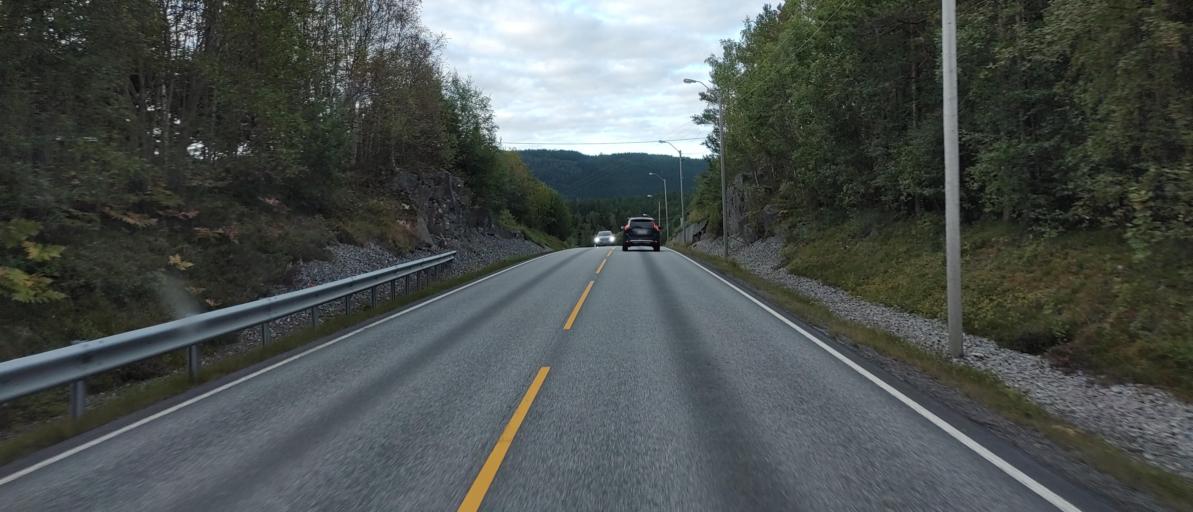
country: NO
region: More og Romsdal
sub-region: Molde
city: Hjelset
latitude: 62.7205
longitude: 7.4295
